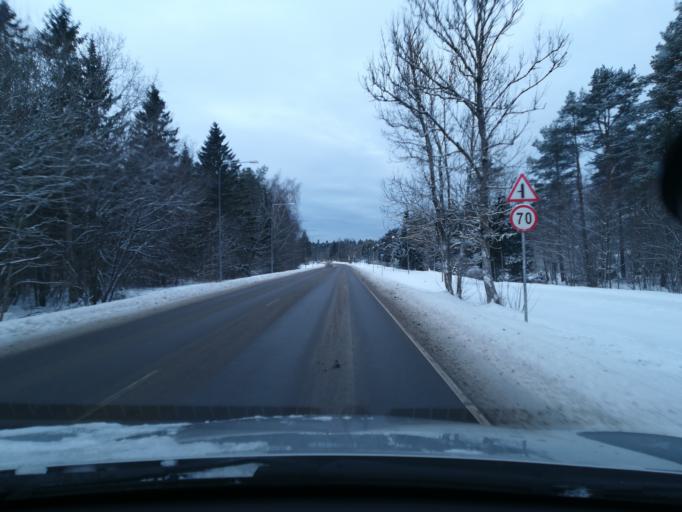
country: EE
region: Harju
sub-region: Harku vald
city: Tabasalu
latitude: 59.4351
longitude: 24.5205
